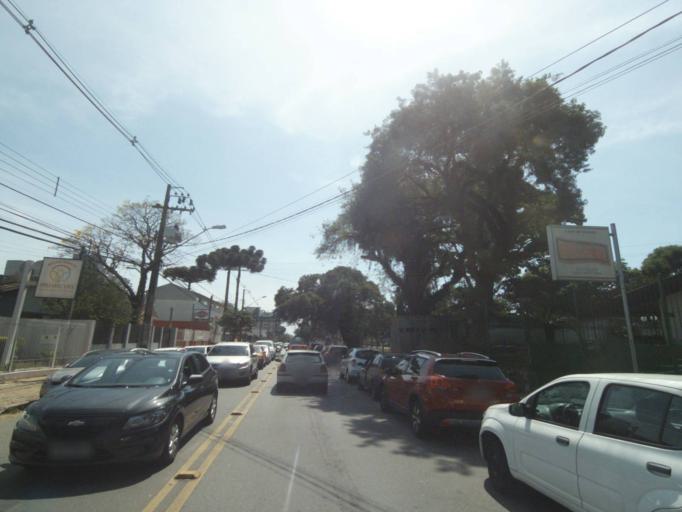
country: BR
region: Parana
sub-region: Curitiba
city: Curitiba
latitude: -25.4726
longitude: -49.2961
